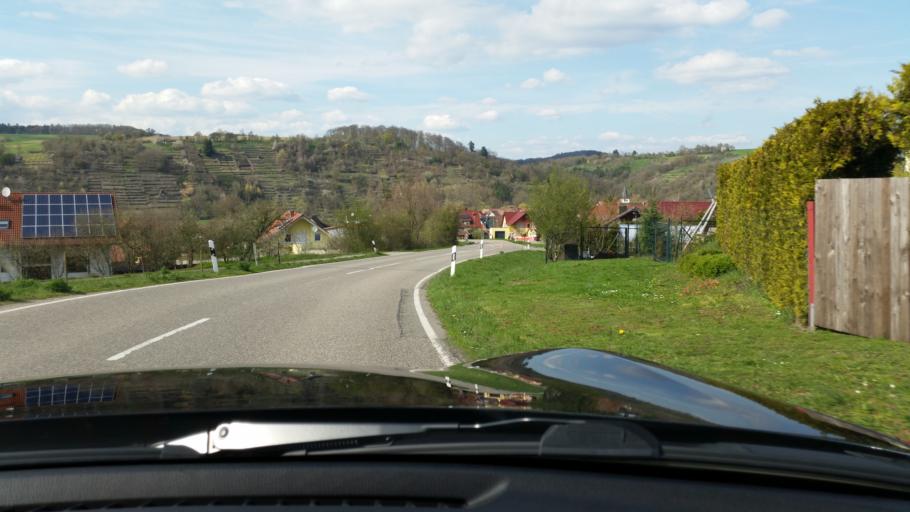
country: DE
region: Baden-Wuerttemberg
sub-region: Regierungsbezirk Stuttgart
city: Neudenau
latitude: 49.2953
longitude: 9.3071
